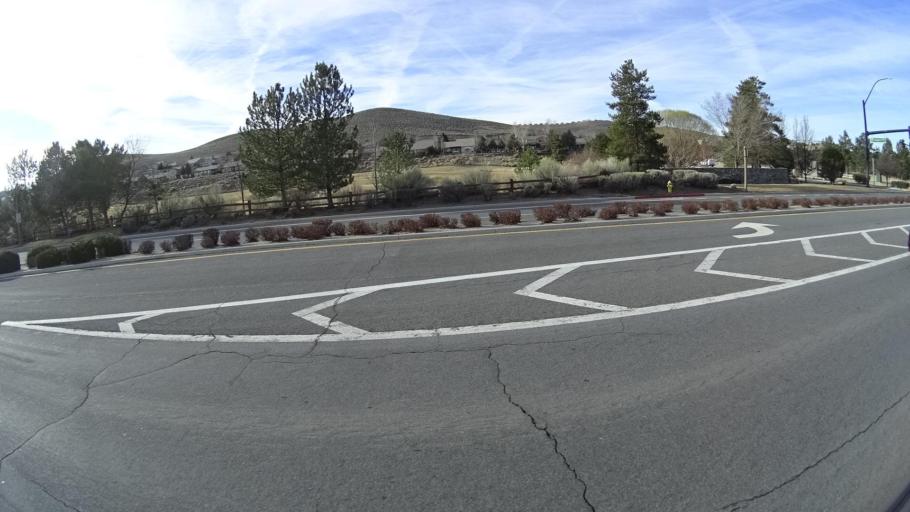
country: US
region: Nevada
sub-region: Washoe County
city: Spanish Springs
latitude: 39.6072
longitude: -119.6854
